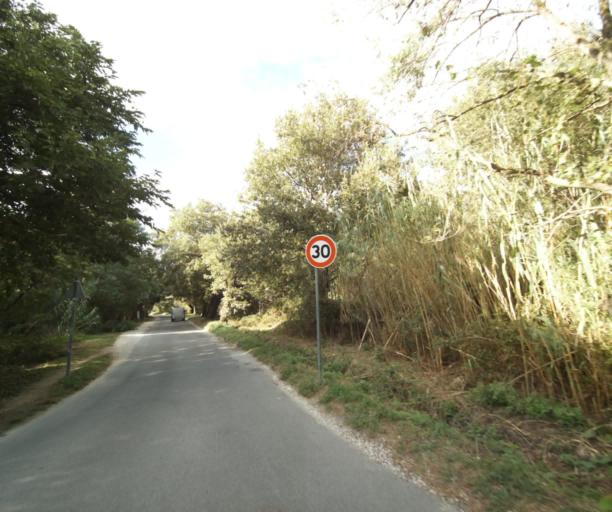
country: FR
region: Languedoc-Roussillon
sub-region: Departement des Pyrenees-Orientales
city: Argelers
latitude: 42.5415
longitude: 3.0415
